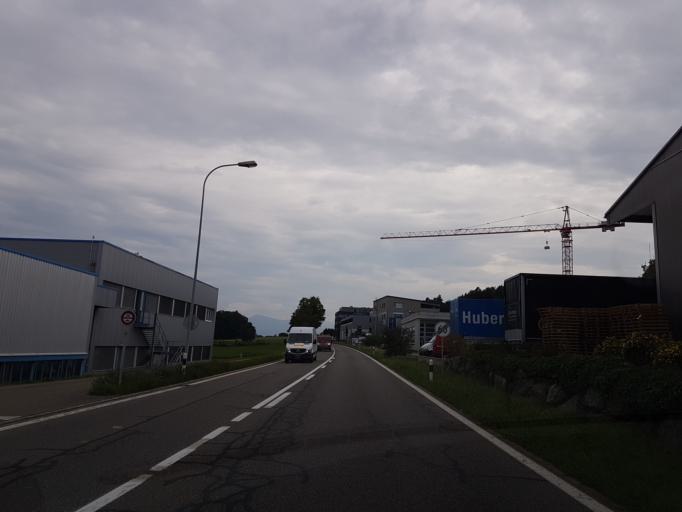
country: CH
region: Aargau
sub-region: Bezirk Muri
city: Muri
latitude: 47.2614
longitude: 8.3529
